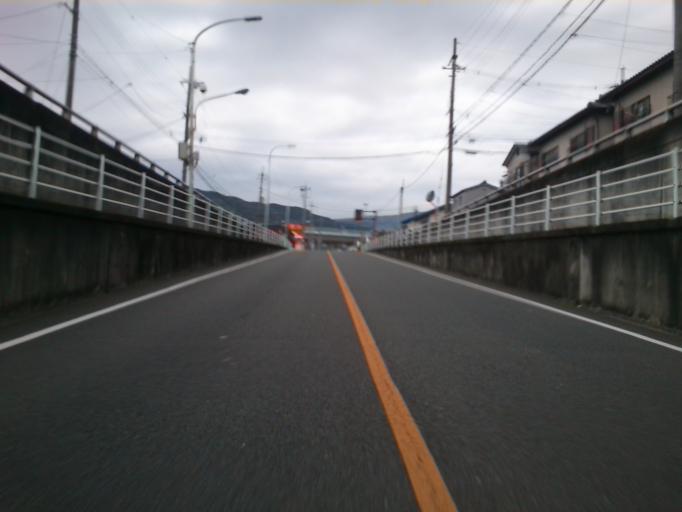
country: JP
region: Kyoto
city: Yawata
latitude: 34.9115
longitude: 135.6938
